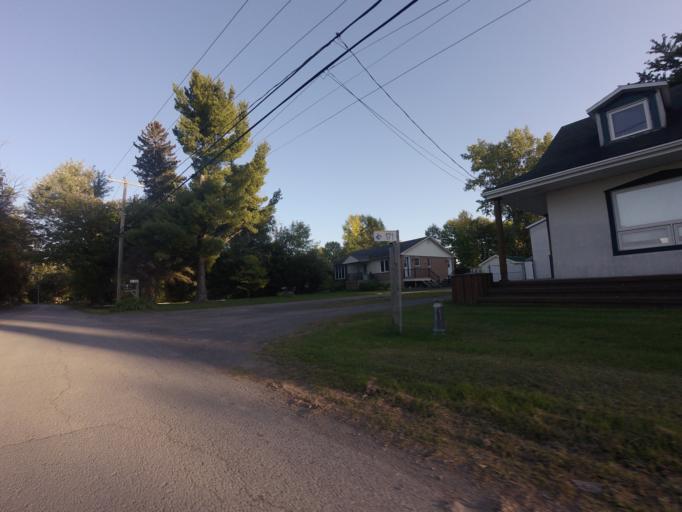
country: CA
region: Quebec
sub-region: Monteregie
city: Rigaud
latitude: 45.4781
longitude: -74.2360
